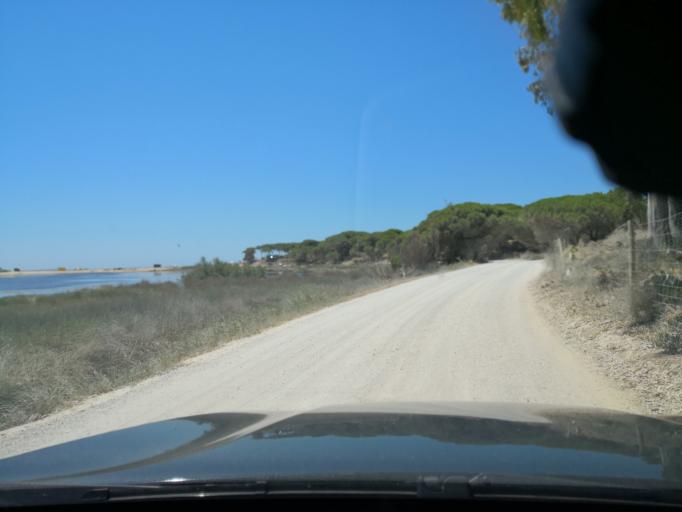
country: PT
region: Faro
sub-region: Loule
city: Quarteira
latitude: 37.0628
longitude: -8.0835
